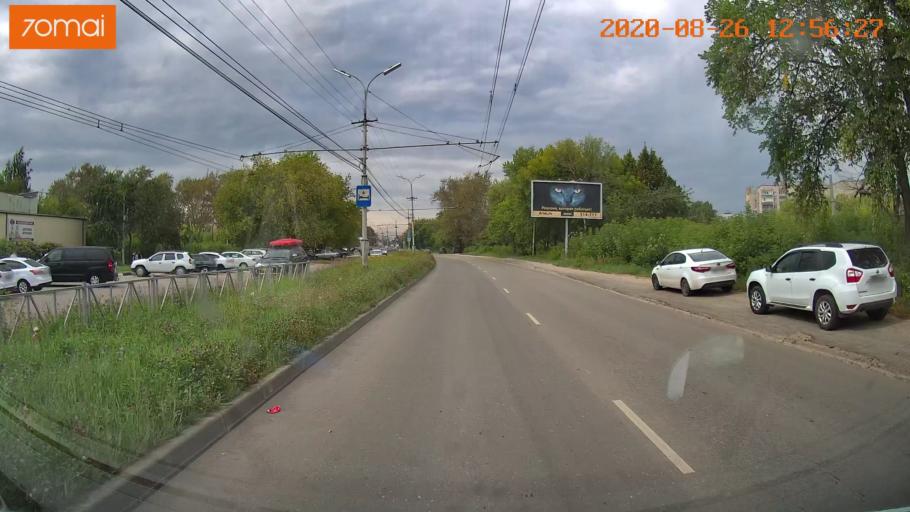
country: RU
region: Rjazan
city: Ryazan'
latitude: 54.6136
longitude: 39.7499
